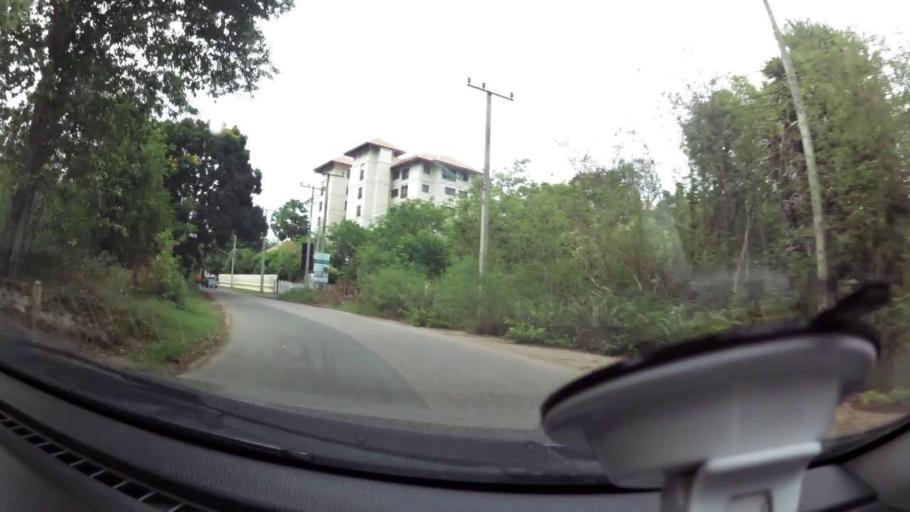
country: TH
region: Prachuap Khiri Khan
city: Pran Buri
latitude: 12.4254
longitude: 99.9795
